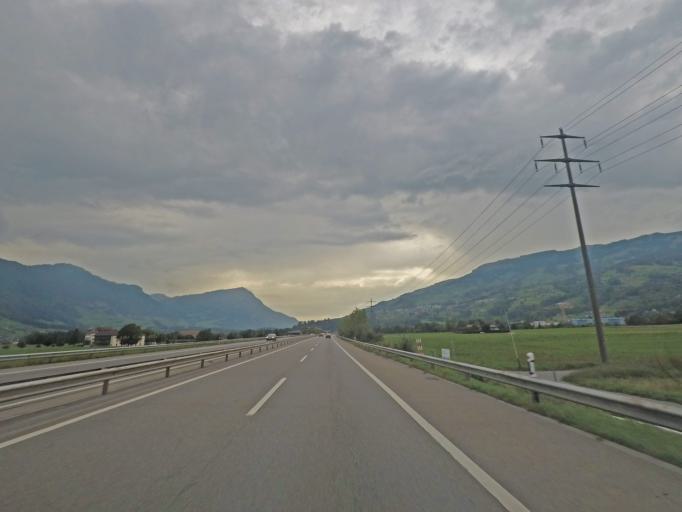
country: CH
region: Schwyz
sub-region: Bezirk Schwyz
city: Steinen
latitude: 47.0404
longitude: 8.6101
